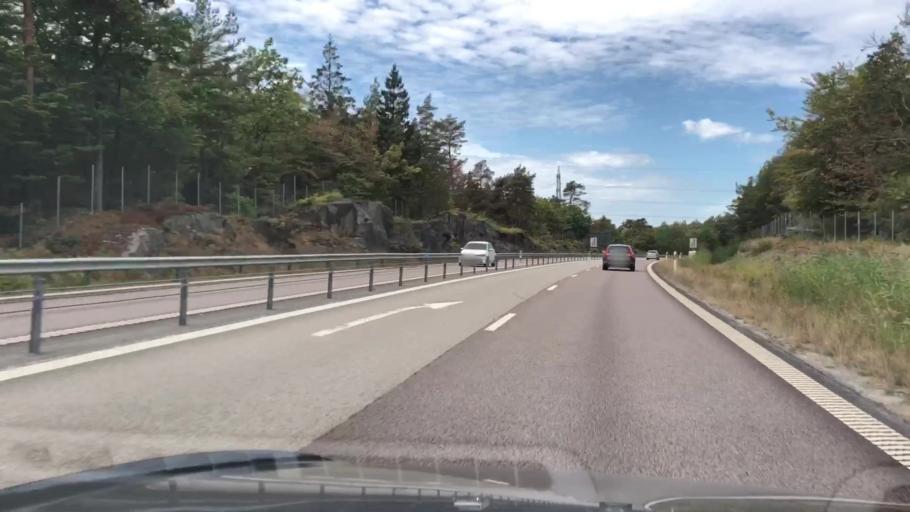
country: SE
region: Blekinge
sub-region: Karlskrona Kommun
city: Rodeby
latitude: 56.2063
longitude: 15.6269
